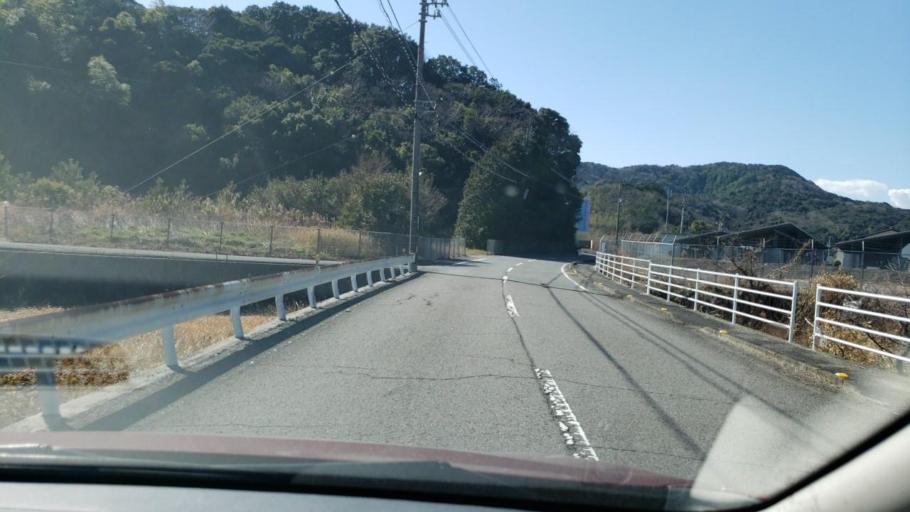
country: JP
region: Tokushima
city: Narutocho-mitsuishi
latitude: 34.2209
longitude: 134.5661
